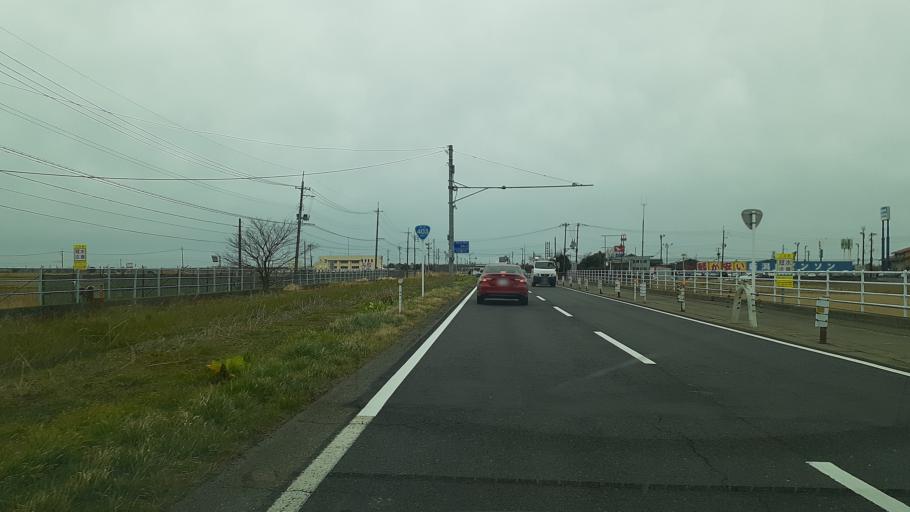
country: JP
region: Niigata
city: Niitsu-honcho
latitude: 37.8132
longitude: 139.1004
